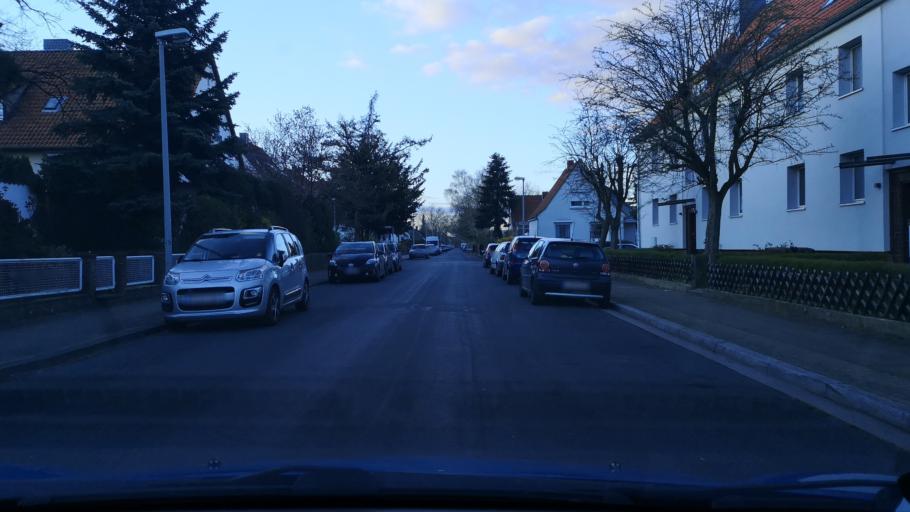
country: DE
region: Lower Saxony
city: Langenhagen
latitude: 52.4107
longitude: 9.7872
